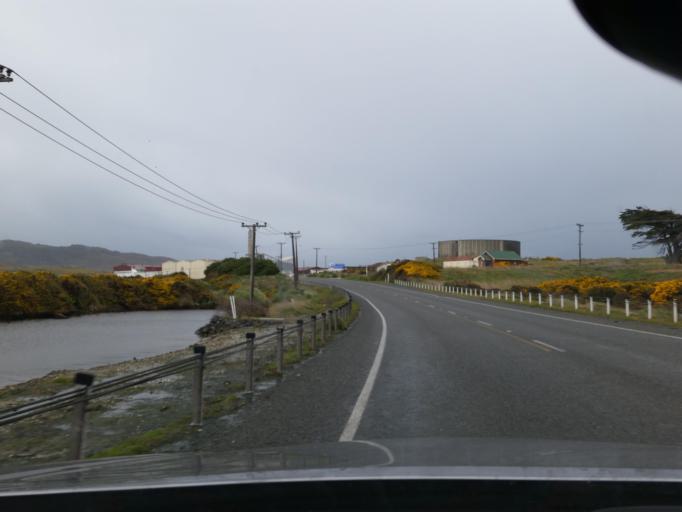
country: NZ
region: Southland
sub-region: Invercargill City
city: Bluff
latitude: -46.5865
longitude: 168.3049
